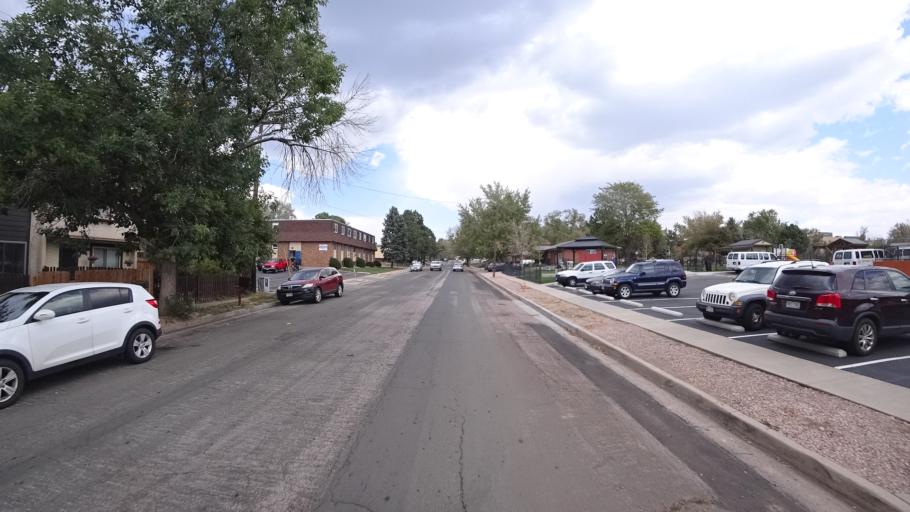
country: US
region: Colorado
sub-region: El Paso County
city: Cimarron Hills
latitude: 38.8489
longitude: -104.7597
